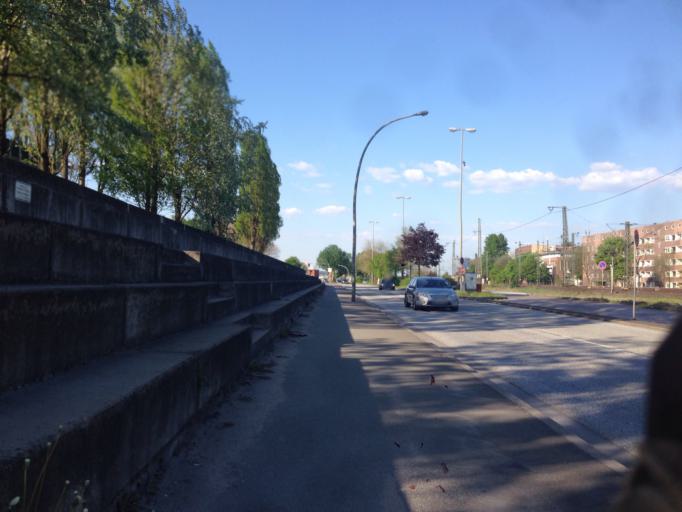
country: DE
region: Hamburg
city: Kleiner Grasbrook
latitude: 53.5258
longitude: 10.0153
